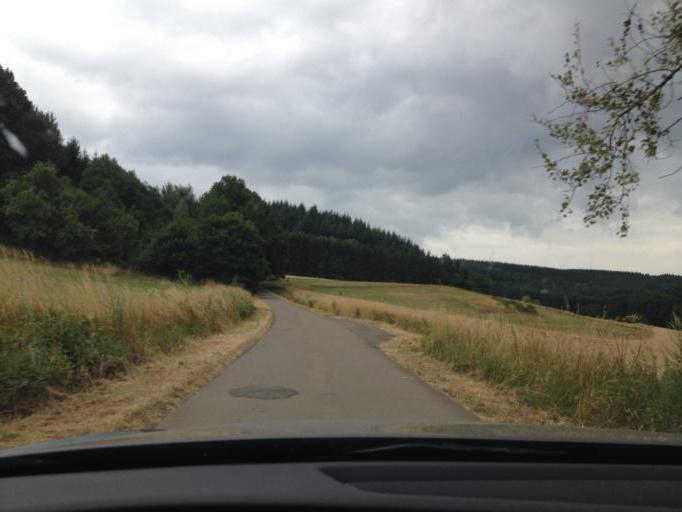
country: DE
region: Saarland
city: Mainzweiler
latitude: 49.4383
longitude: 7.1152
